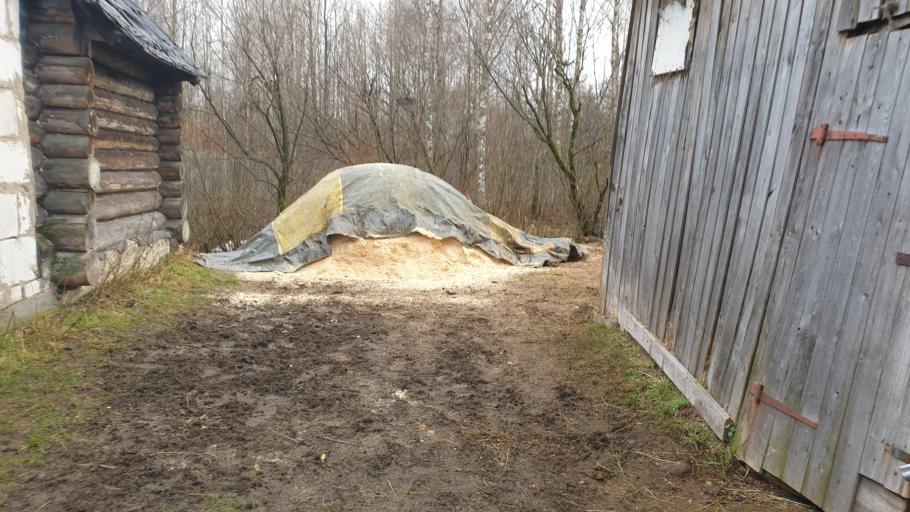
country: RU
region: Kirov
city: Kirs
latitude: 59.3356
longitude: 52.2407
